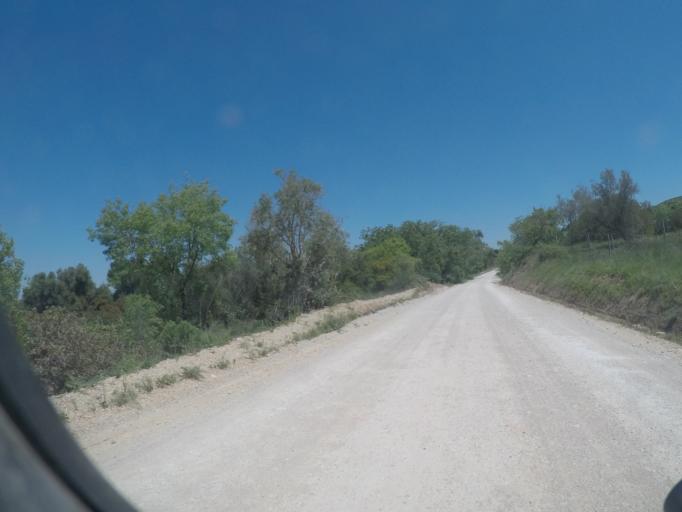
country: PT
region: Setubal
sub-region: Sesimbra
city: Sesimbra
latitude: 38.4647
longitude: -9.0501
